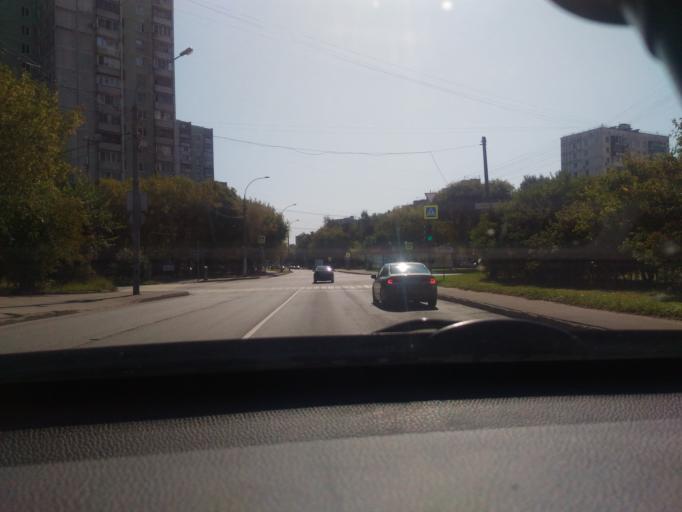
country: RU
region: Moscow
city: Vatutino
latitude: 55.8856
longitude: 37.6863
